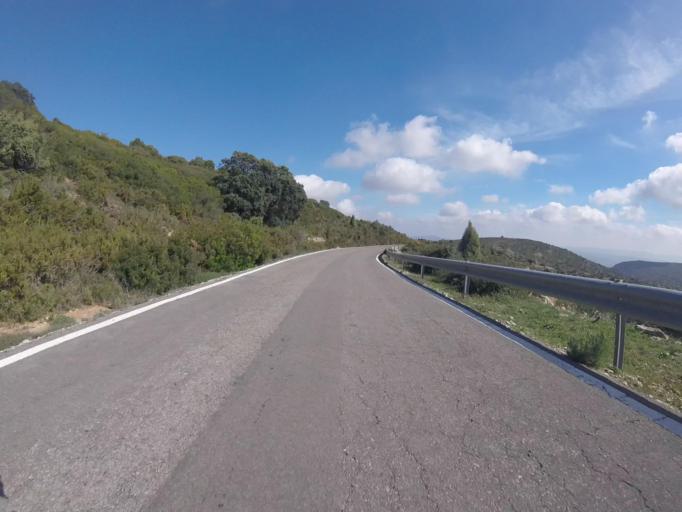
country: ES
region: Valencia
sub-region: Provincia de Castello
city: Albocasser
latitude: 40.3380
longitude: 0.0465
